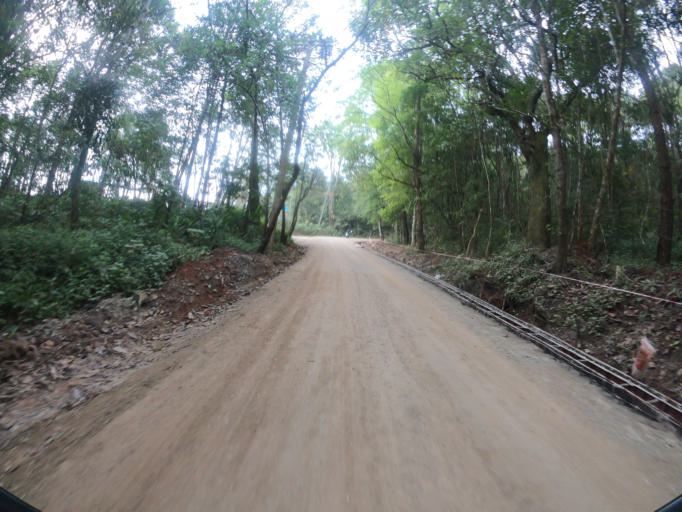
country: TH
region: Chiang Mai
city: Chiang Mai
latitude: 18.8159
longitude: 98.8891
